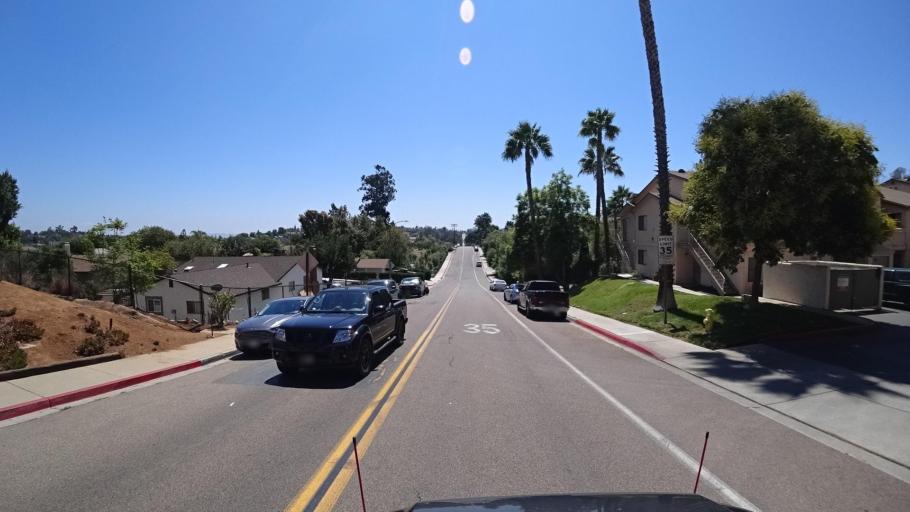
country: US
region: California
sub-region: San Diego County
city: Fallbrook
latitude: 33.3763
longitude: -117.2580
